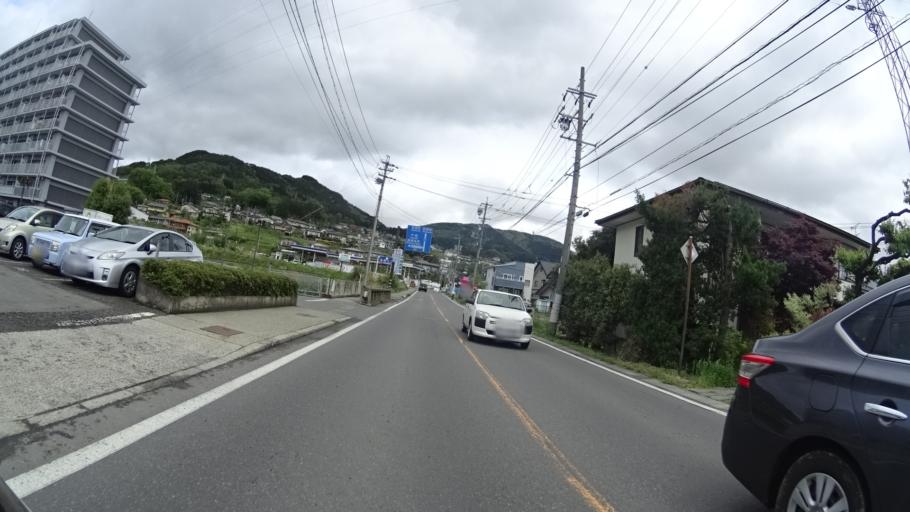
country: JP
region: Nagano
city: Nagano-shi
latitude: 36.6805
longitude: 138.2008
